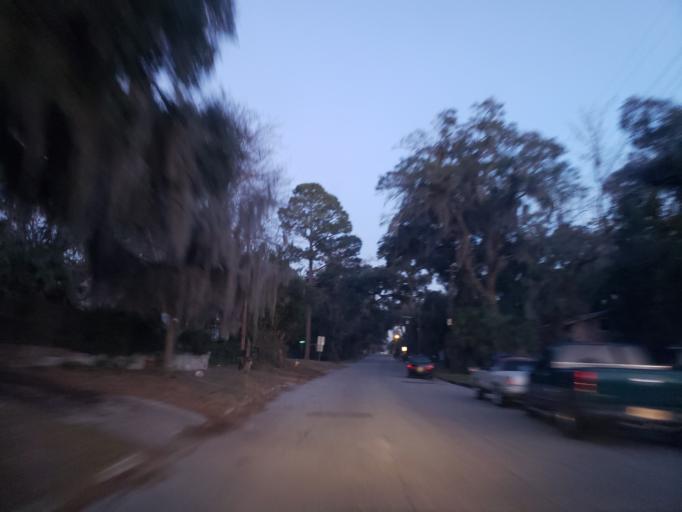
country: US
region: Georgia
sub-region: Chatham County
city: Thunderbolt
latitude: 32.0149
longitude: -81.0641
